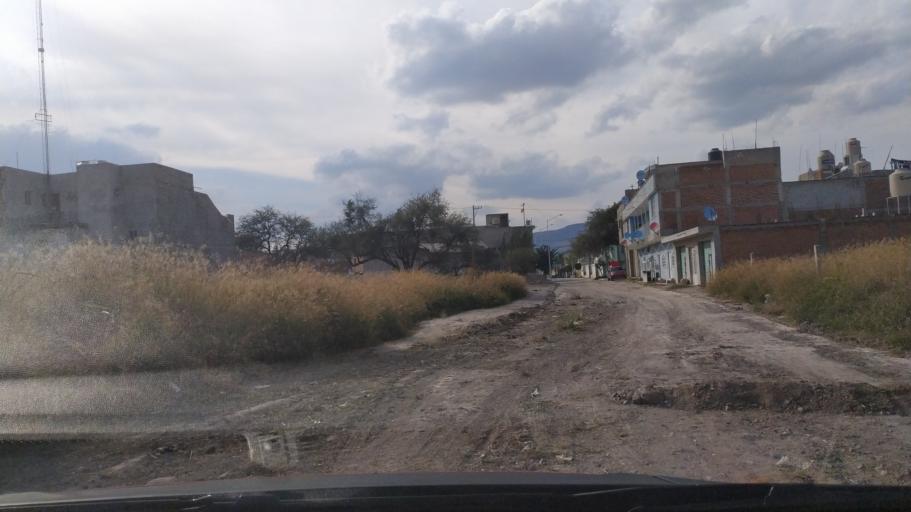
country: MX
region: Guanajuato
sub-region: San Francisco del Rincon
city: Fraccionamiento la Mezquitera
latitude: 21.0053
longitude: -101.8471
